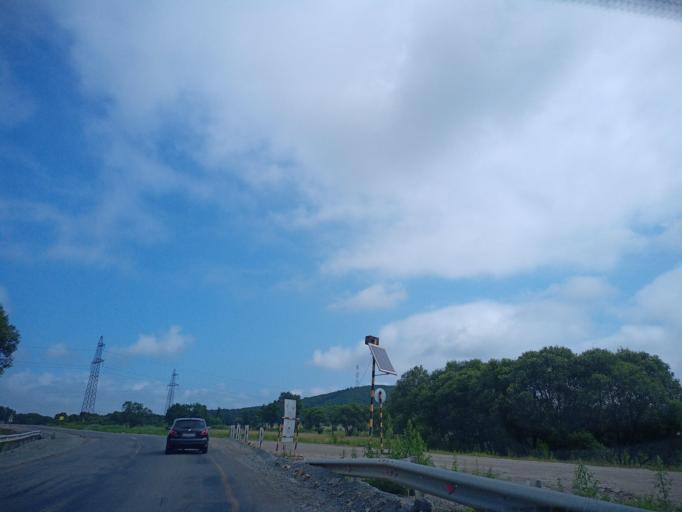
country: RU
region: Primorskiy
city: Dal'nerechensk
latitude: 46.0681
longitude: 133.8950
